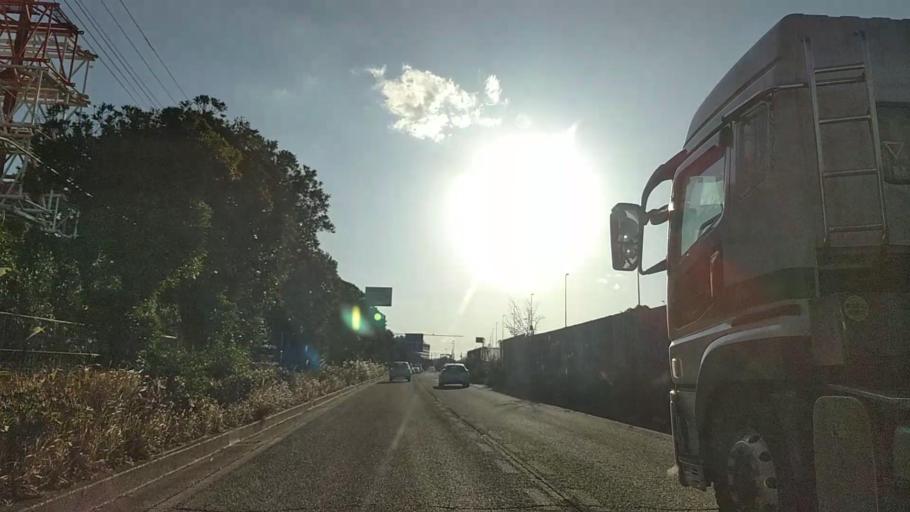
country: JP
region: Tokyo
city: Urayasu
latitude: 35.6626
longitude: 139.9180
